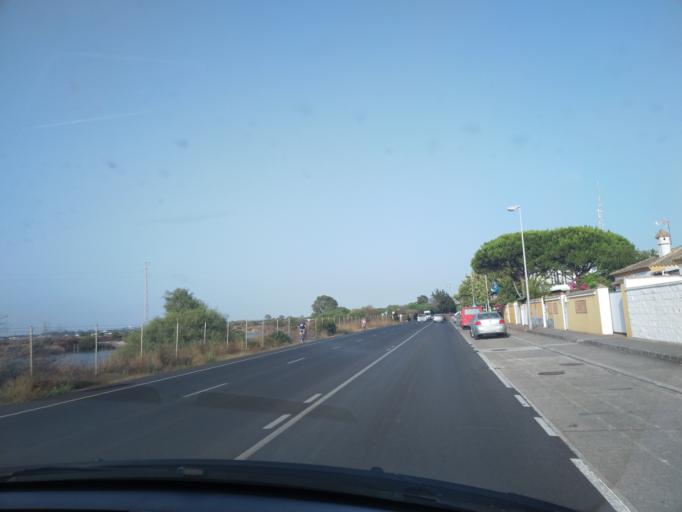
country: ES
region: Andalusia
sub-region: Provincia de Cadiz
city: Chiclana de la Frontera
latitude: 36.3842
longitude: -6.1955
